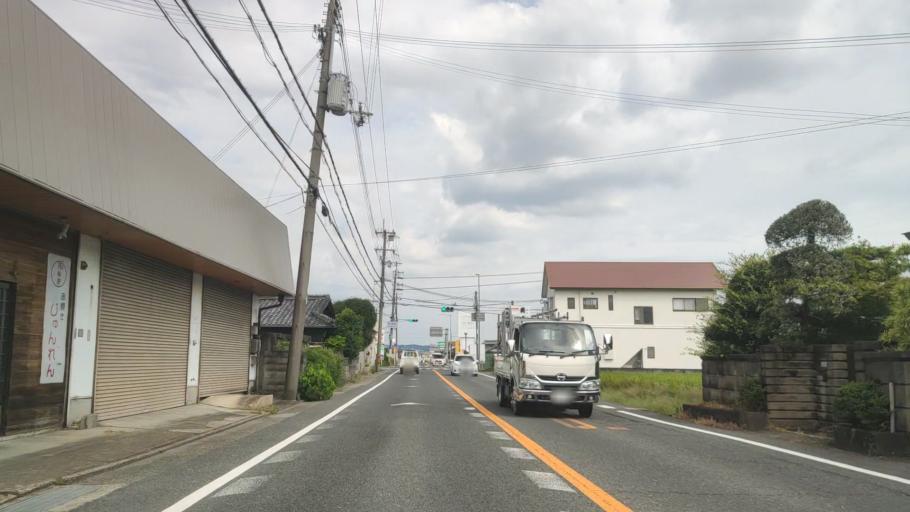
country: JP
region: Wakayama
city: Hashimoto
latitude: 34.2896
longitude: 135.4813
